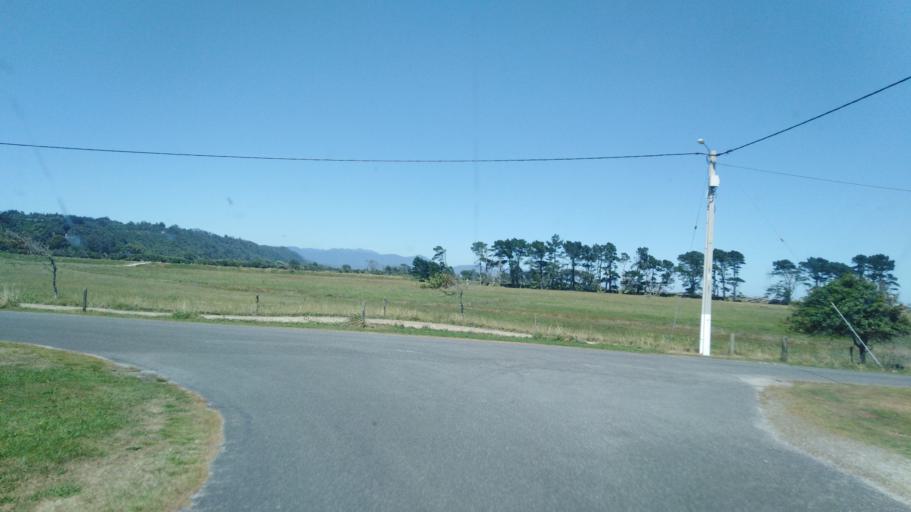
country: NZ
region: West Coast
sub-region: Buller District
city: Westport
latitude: -41.2505
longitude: 172.1091
